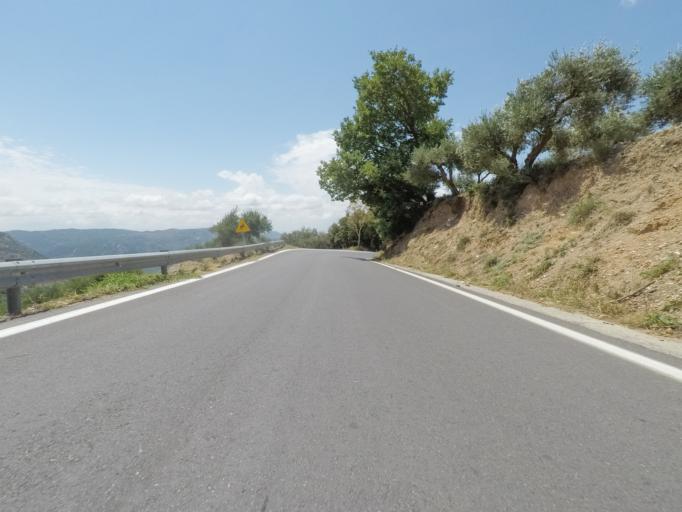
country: GR
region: Crete
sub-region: Nomos Irakleiou
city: Mokhos
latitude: 35.2290
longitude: 25.4590
